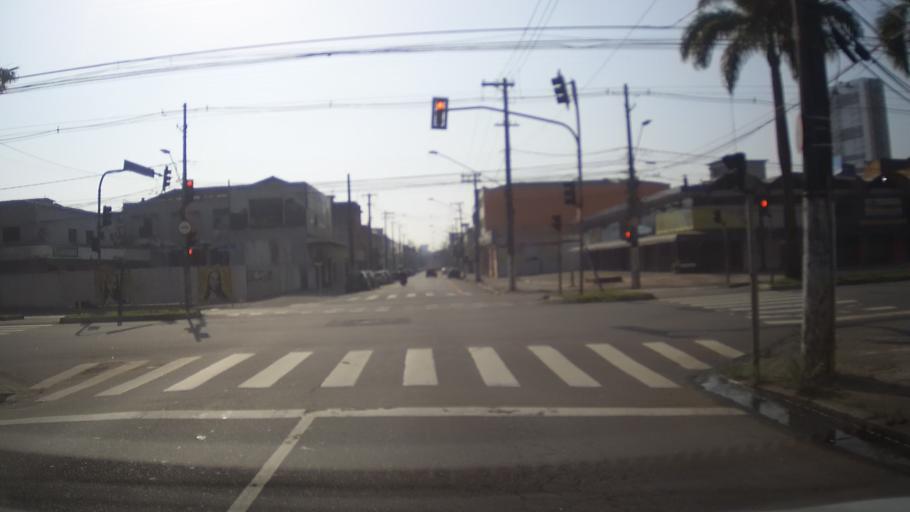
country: BR
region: Sao Paulo
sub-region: Santos
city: Santos
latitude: -23.9451
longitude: -46.3304
